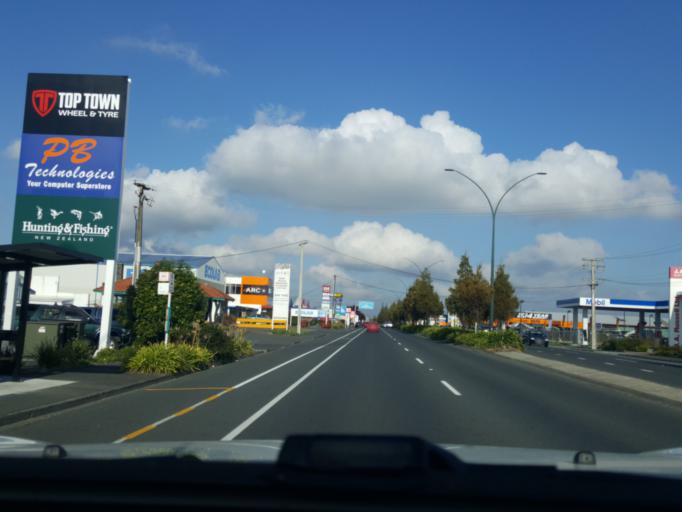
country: NZ
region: Waikato
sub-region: Hamilton City
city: Hamilton
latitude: -37.7551
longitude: 175.2435
